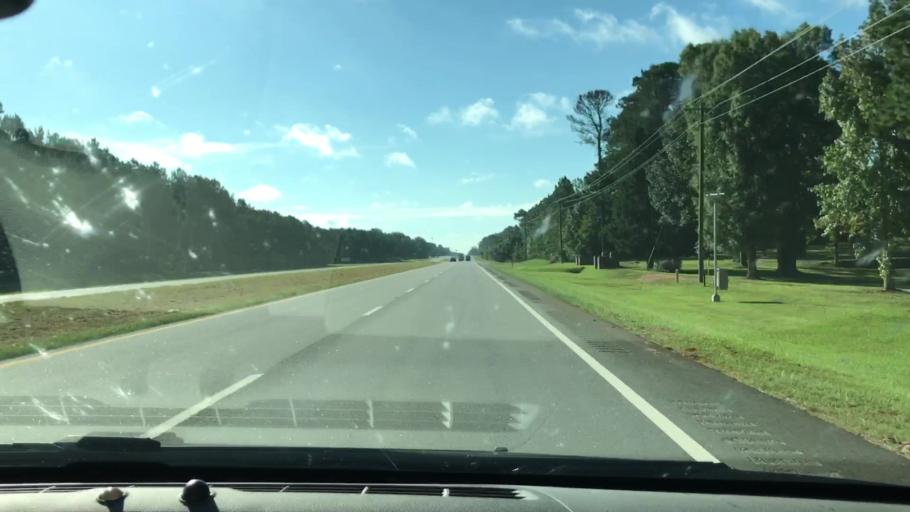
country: US
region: Georgia
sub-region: Lee County
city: Leesburg
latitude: 31.6754
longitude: -84.2940
